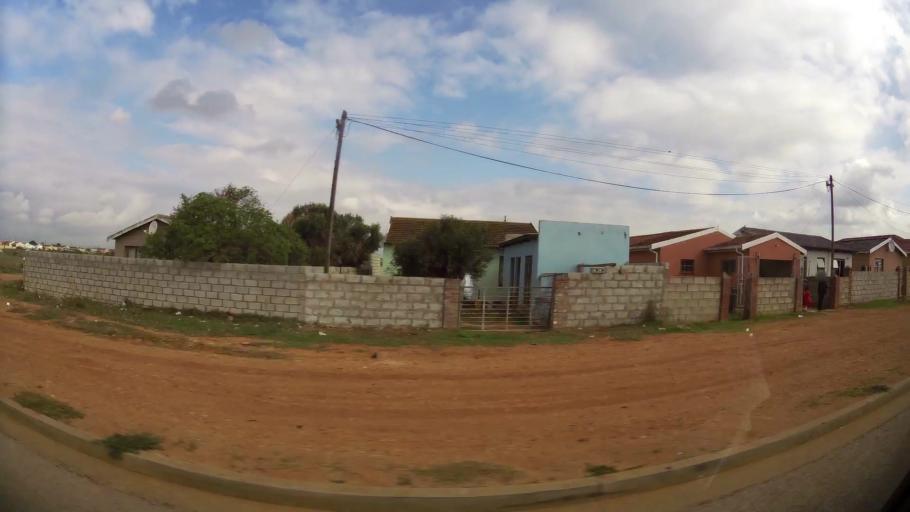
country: ZA
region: Eastern Cape
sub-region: Nelson Mandela Bay Metropolitan Municipality
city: Port Elizabeth
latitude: -33.8164
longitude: 25.5941
